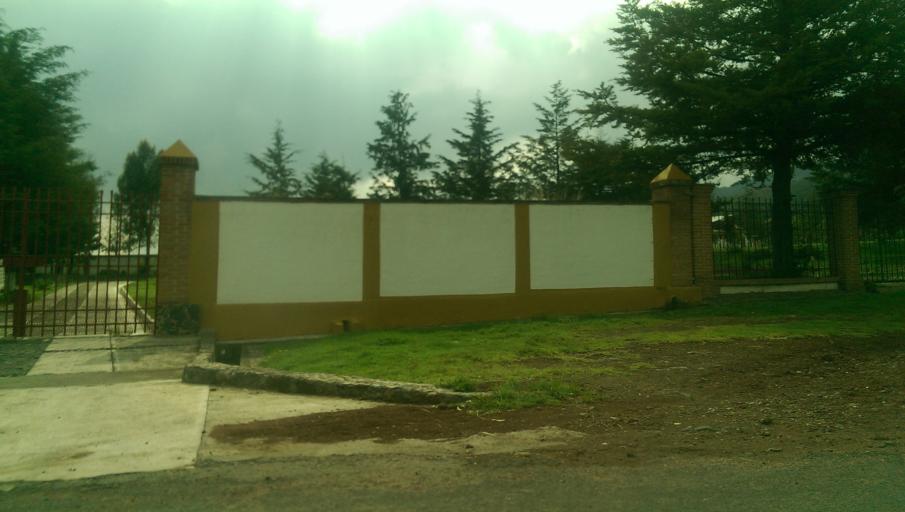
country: MX
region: Mexico
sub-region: Jilotepec
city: Jilotepec de Molina Enriquez
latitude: 19.9352
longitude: -99.4926
